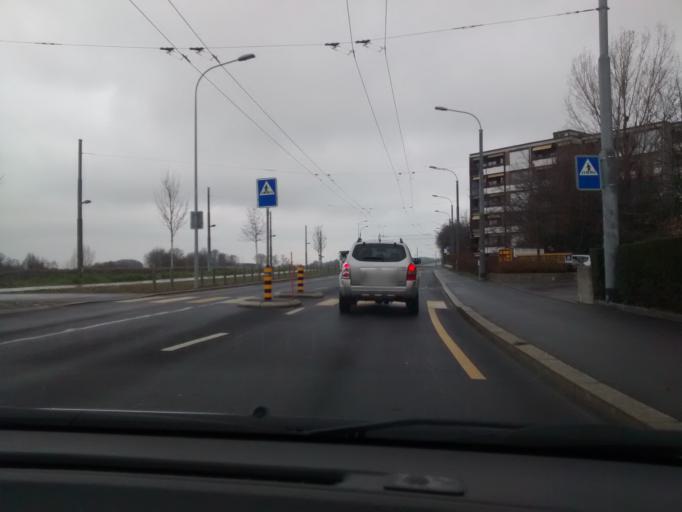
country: CH
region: Vaud
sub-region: Lausanne District
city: Blecherette
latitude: 46.5384
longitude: 6.6173
